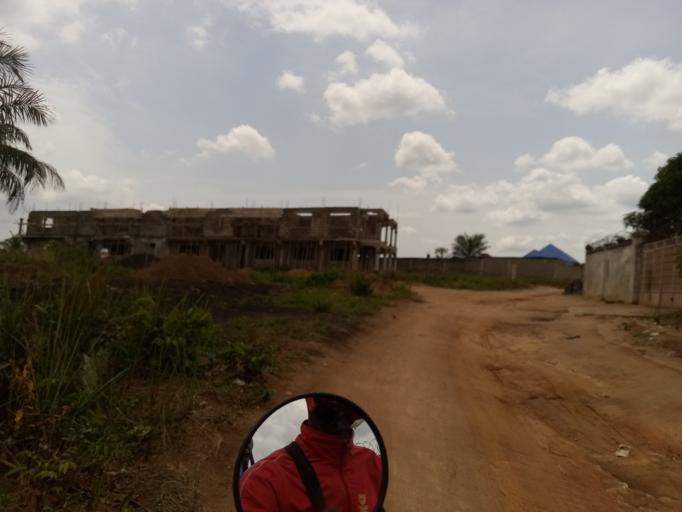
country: SL
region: Western Area
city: Waterloo
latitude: 8.3302
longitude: -13.0320
